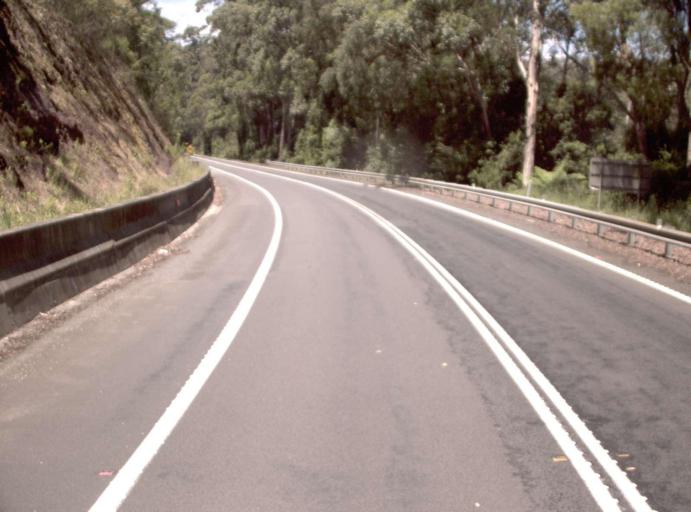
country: AU
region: New South Wales
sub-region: Bombala
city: Bombala
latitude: -37.6083
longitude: 148.8977
